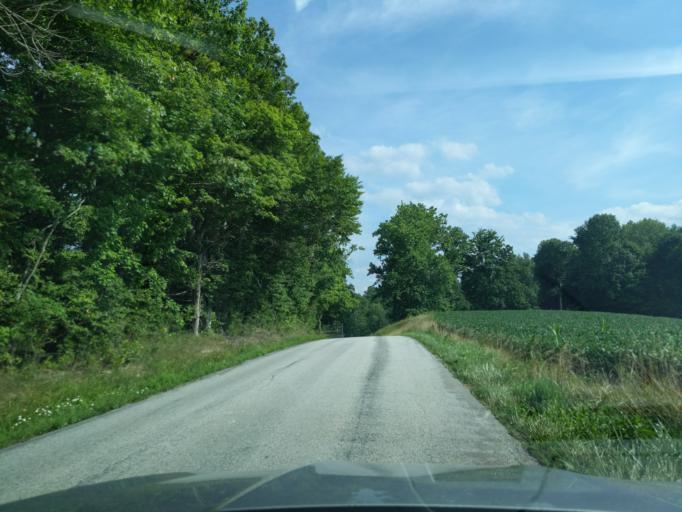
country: US
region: Indiana
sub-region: Decatur County
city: Greensburg
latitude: 39.2482
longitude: -85.4697
